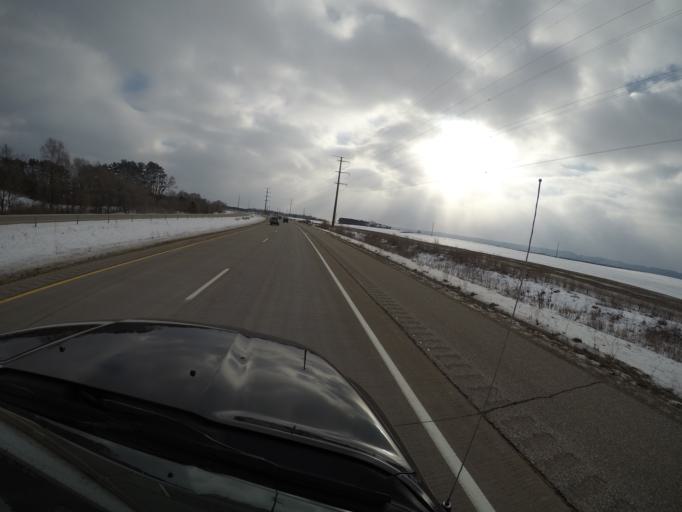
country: US
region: Wisconsin
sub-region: La Crosse County
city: Brice Prairie
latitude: 43.9621
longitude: -91.2859
